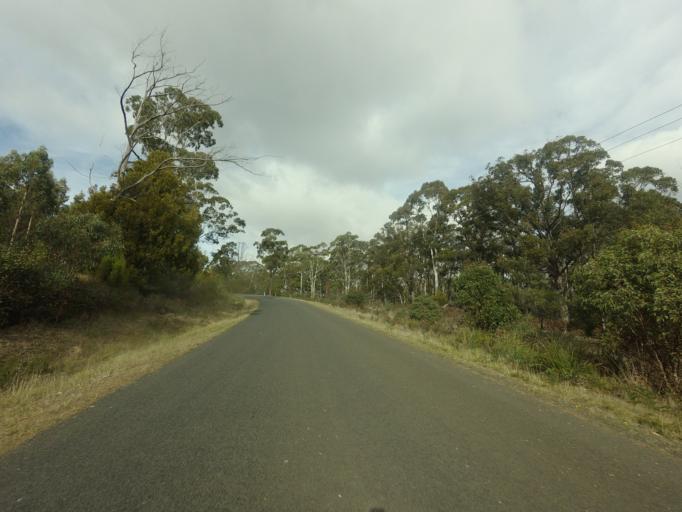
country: AU
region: Tasmania
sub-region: Brighton
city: Bridgewater
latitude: -42.4149
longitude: 147.4092
